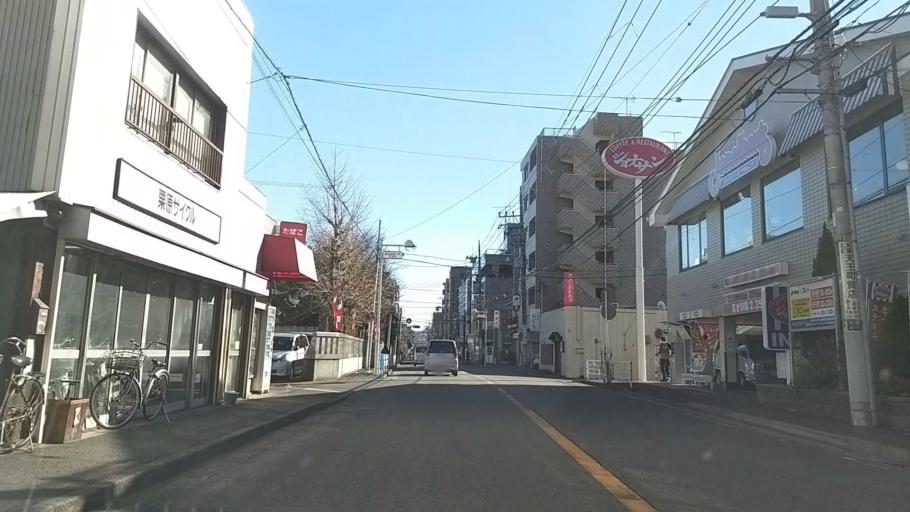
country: JP
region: Kanagawa
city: Yokohama
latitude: 35.4557
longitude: 139.6029
